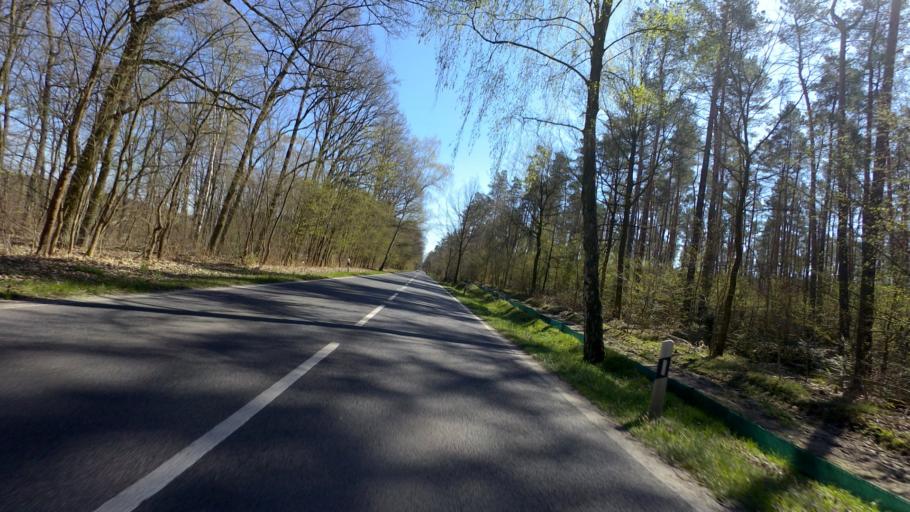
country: DE
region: Brandenburg
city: Schulzendorf
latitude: 52.3402
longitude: 13.5754
